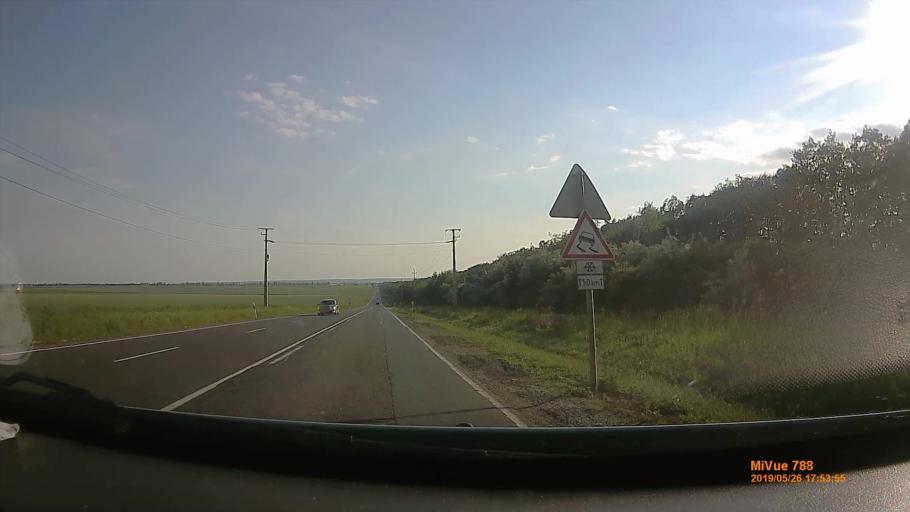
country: HU
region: Borsod-Abauj-Zemplen
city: Arnot
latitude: 48.1475
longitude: 20.8918
